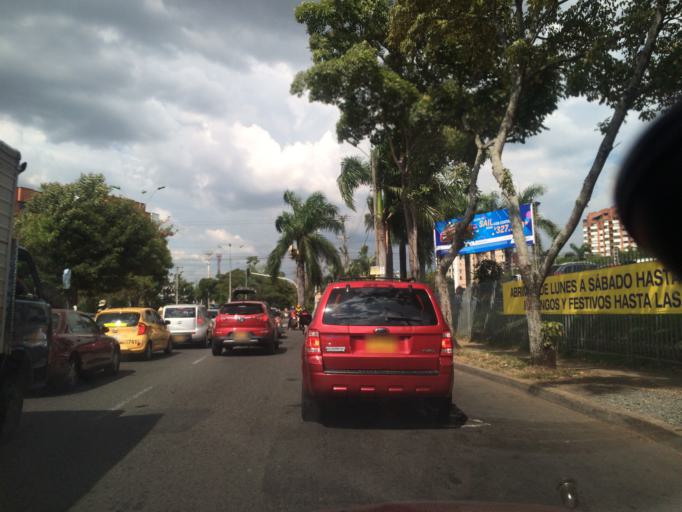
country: CO
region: Valle del Cauca
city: Cali
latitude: 3.3934
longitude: -76.5390
